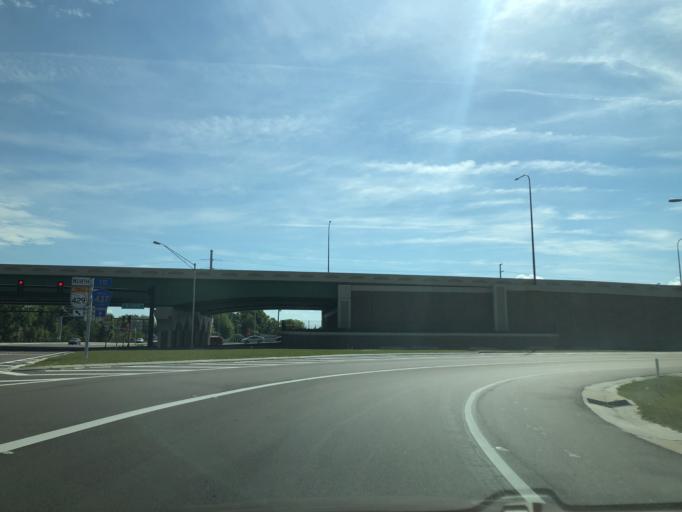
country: US
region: Florida
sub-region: Orange County
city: Zellwood
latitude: 28.6980
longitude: -81.5601
